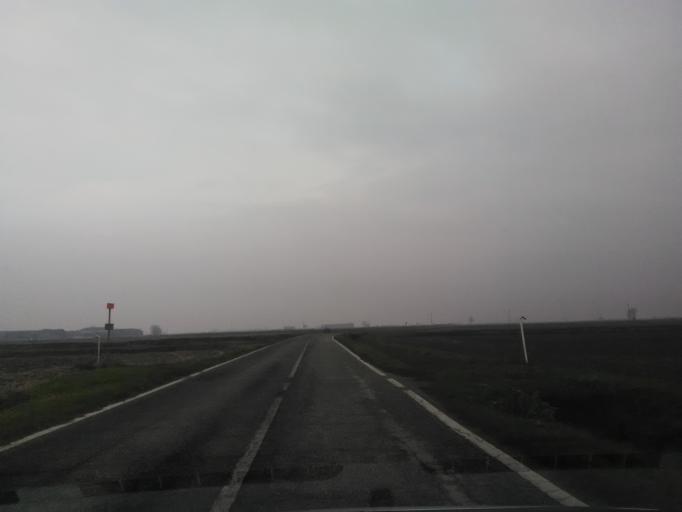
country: IT
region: Piedmont
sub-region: Provincia di Vercelli
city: Salasco
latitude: 45.2992
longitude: 8.2690
